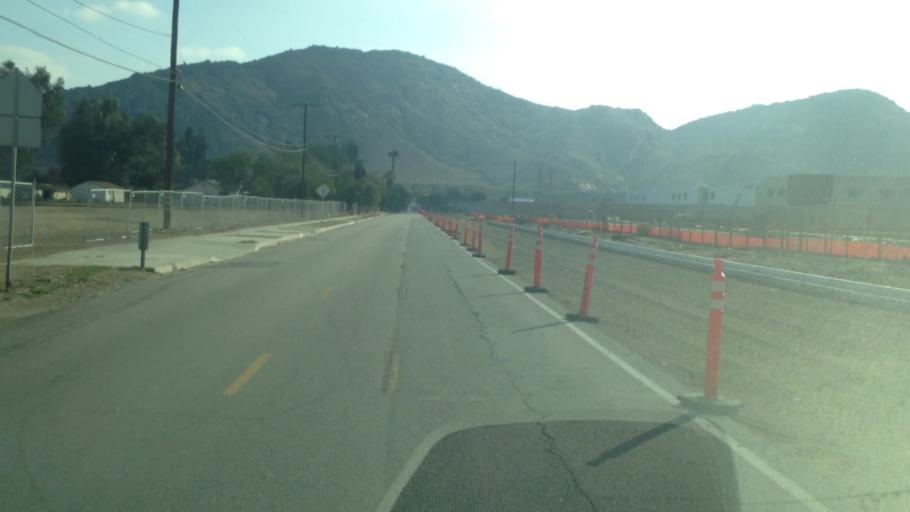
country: US
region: California
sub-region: San Bernardino County
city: Fontana
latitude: 34.0554
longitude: -117.4443
